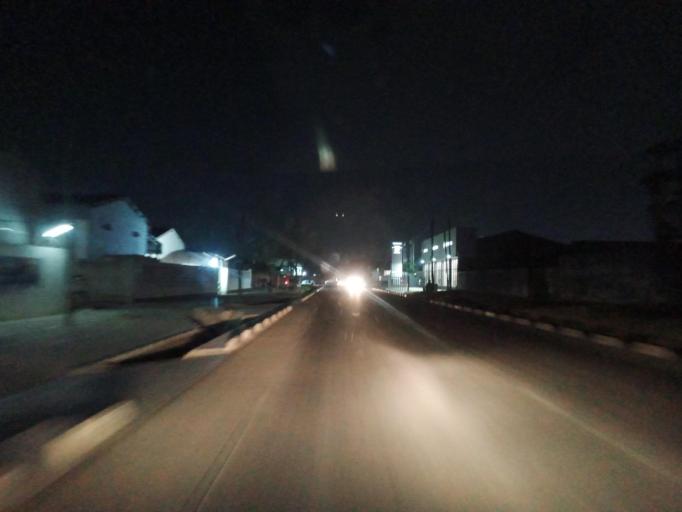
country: ZM
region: Lusaka
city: Lusaka
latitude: -15.3936
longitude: 28.2709
